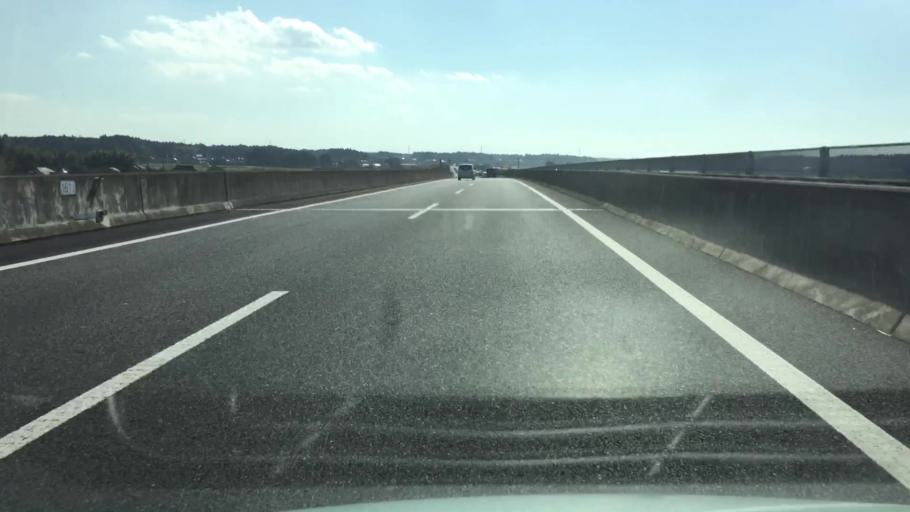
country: JP
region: Ibaraki
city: Tomobe
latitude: 36.3275
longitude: 140.2950
